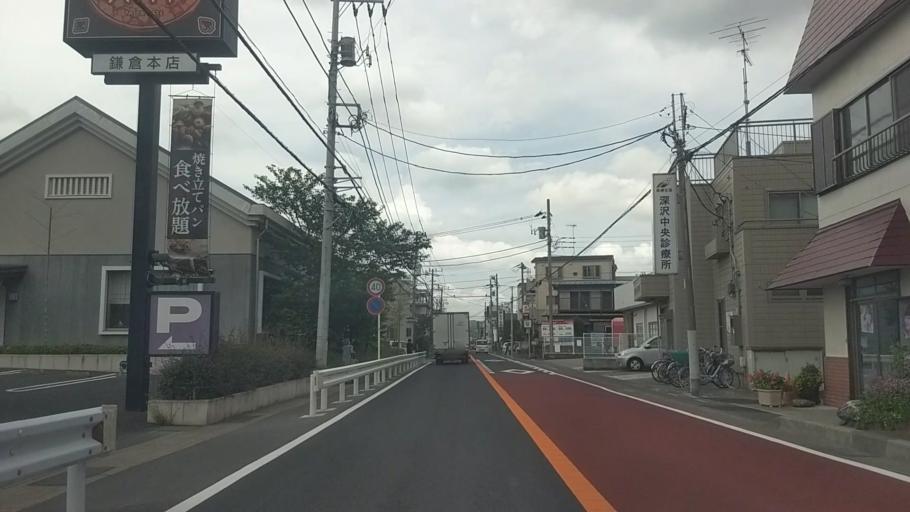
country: JP
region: Kanagawa
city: Fujisawa
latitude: 35.3284
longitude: 139.5094
